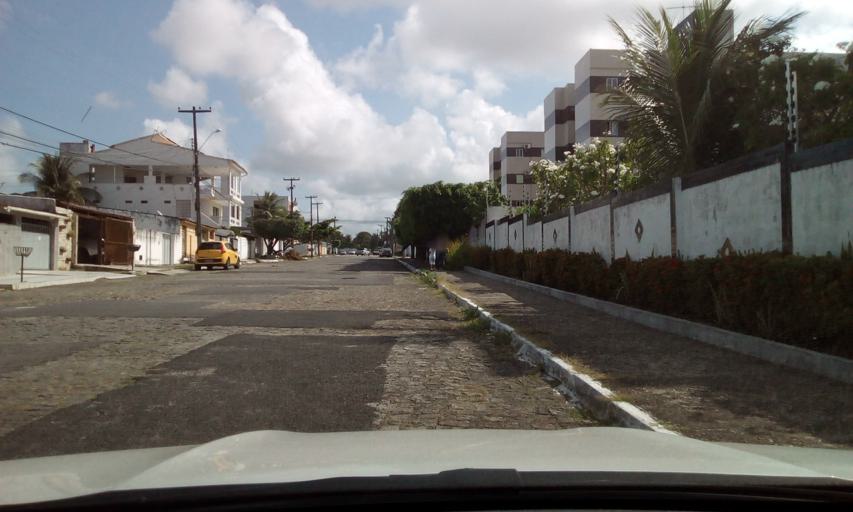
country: BR
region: Paraiba
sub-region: Joao Pessoa
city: Joao Pessoa
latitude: -7.1436
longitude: -34.8352
